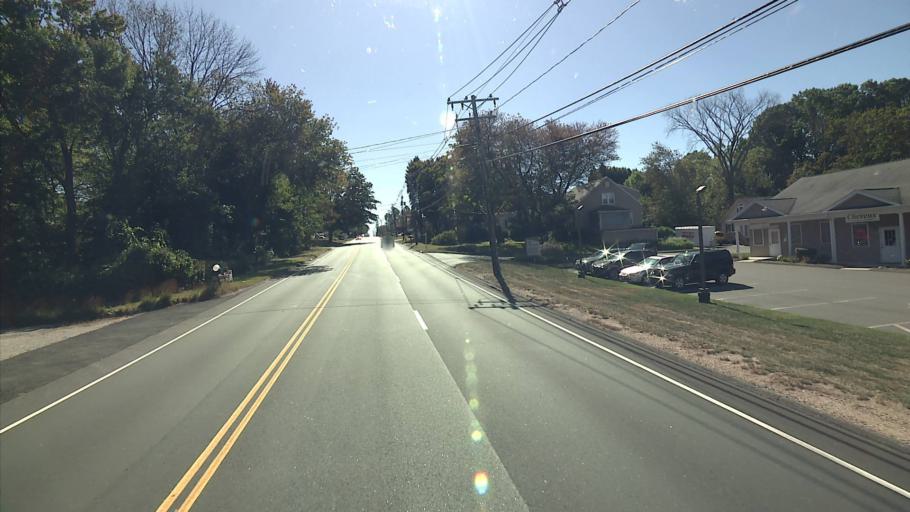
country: US
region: Connecticut
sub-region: New Haven County
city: Prospect
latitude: 41.5193
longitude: -72.9909
